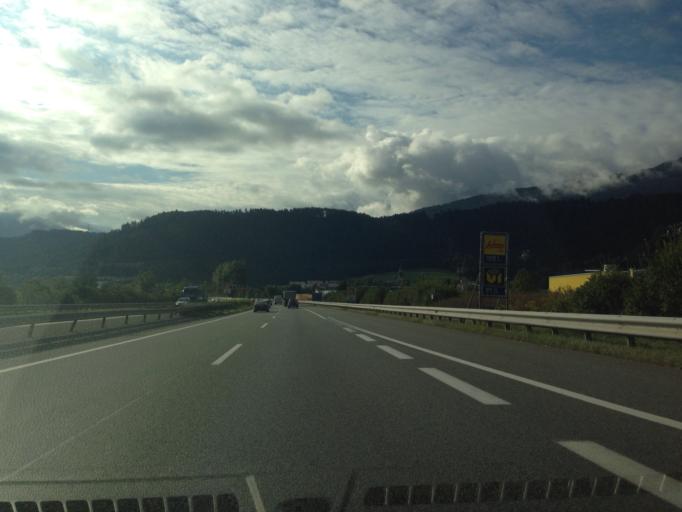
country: AT
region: Tyrol
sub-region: Politischer Bezirk Innsbruck Land
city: Vols
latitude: 47.2586
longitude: 11.3246
